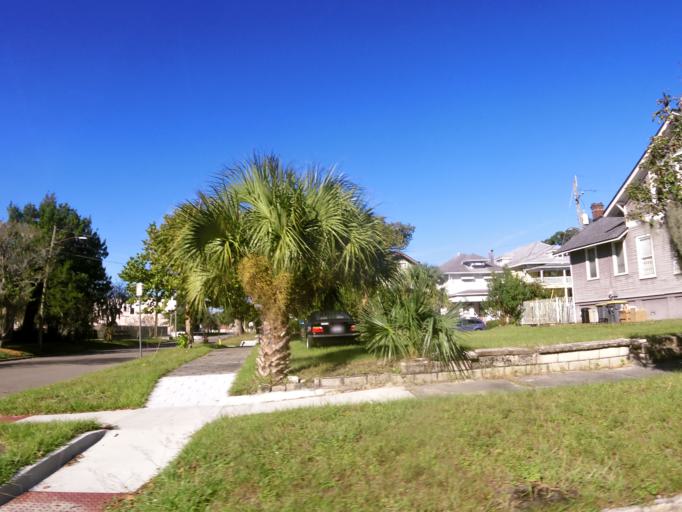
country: US
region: Florida
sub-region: Duval County
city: Jacksonville
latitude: 30.3489
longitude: -81.6597
